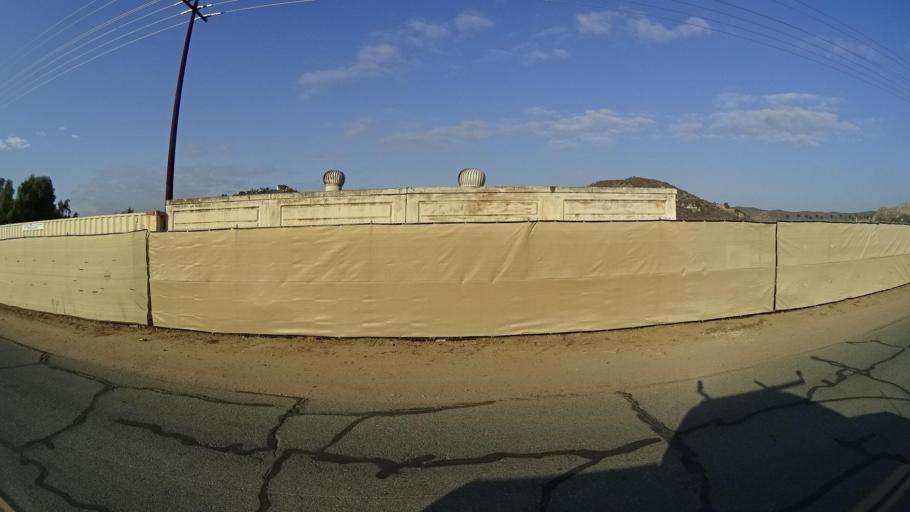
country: US
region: California
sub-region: San Diego County
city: Eucalyptus Hills
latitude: 32.8995
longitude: -116.9304
